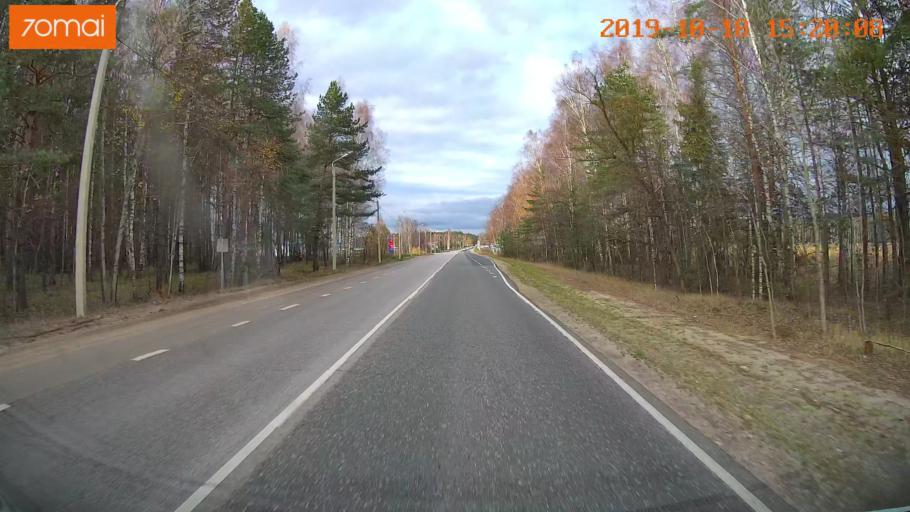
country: RU
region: Vladimir
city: Anopino
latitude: 55.6832
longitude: 40.7428
